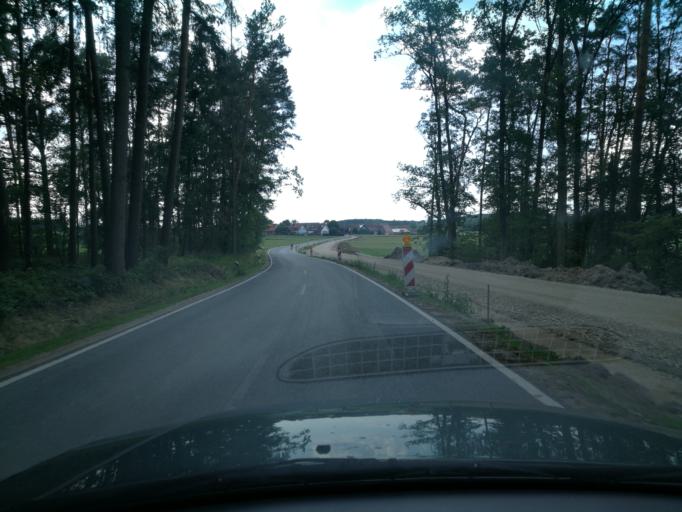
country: DE
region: Bavaria
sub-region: Regierungsbezirk Mittelfranken
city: Cadolzburg
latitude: 49.4798
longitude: 10.8559
